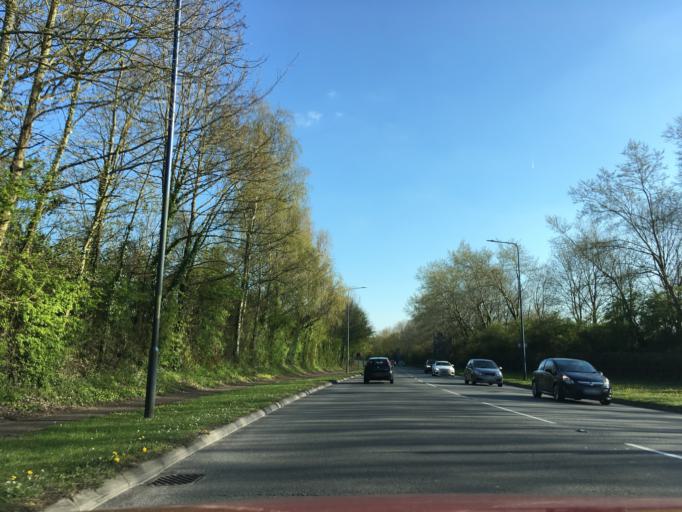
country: GB
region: Wales
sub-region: Torfaen County Borough
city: Cwmbran
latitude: 51.6343
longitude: -3.0198
